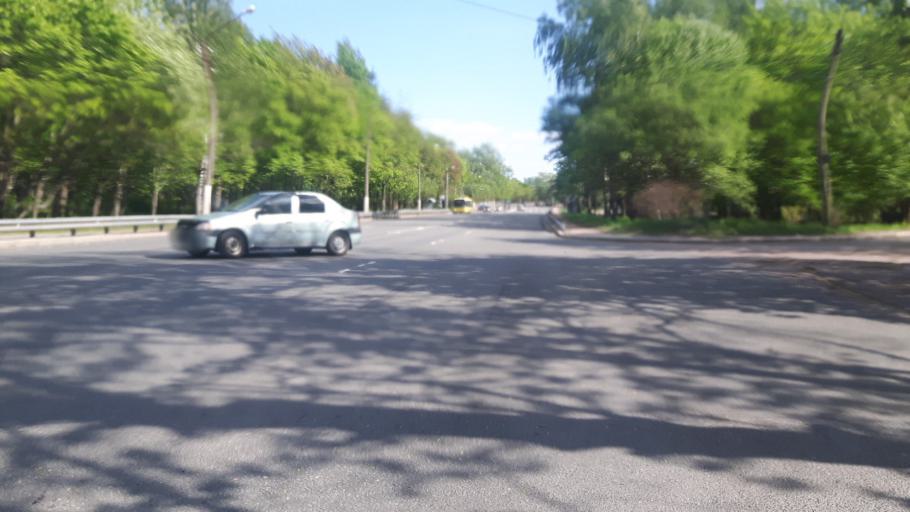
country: RU
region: Leningrad
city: Vyborg
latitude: 60.7291
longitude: 28.7009
